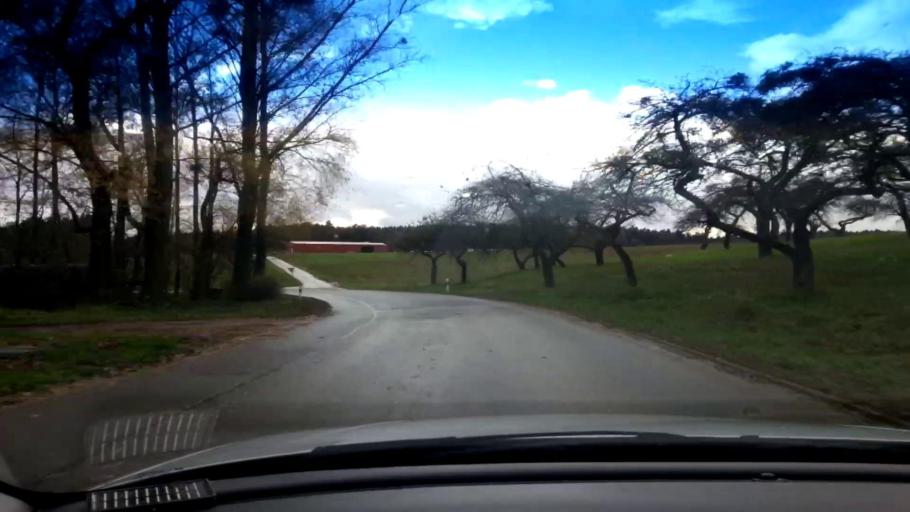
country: DE
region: Bavaria
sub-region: Upper Franconia
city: Zapfendorf
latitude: 50.0209
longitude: 10.9667
